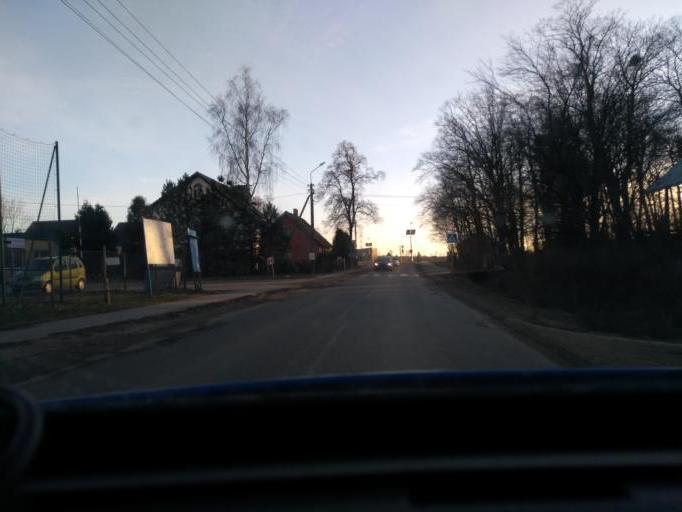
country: PL
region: Pomeranian Voivodeship
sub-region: Powiat kartuski
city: Przodkowo
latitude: 54.4005
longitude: 18.3317
